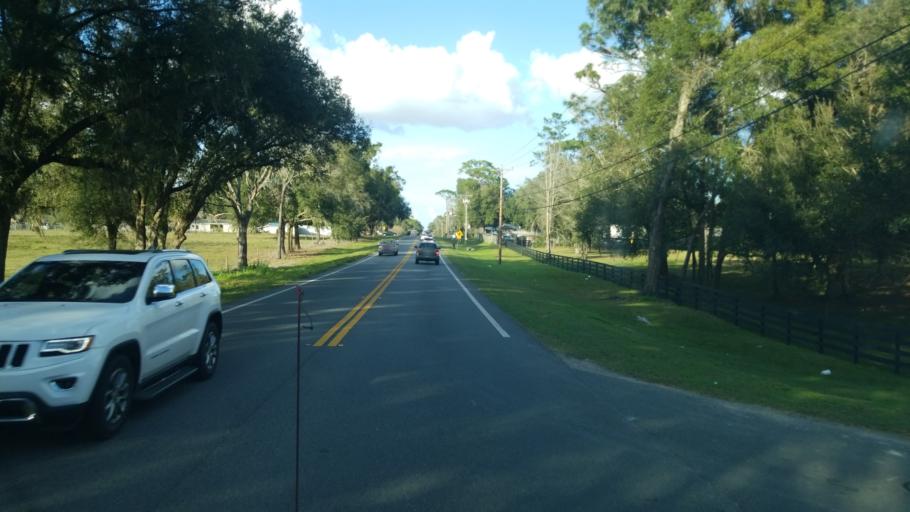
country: US
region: Florida
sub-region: Marion County
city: Ocala
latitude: 29.2280
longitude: -82.1225
